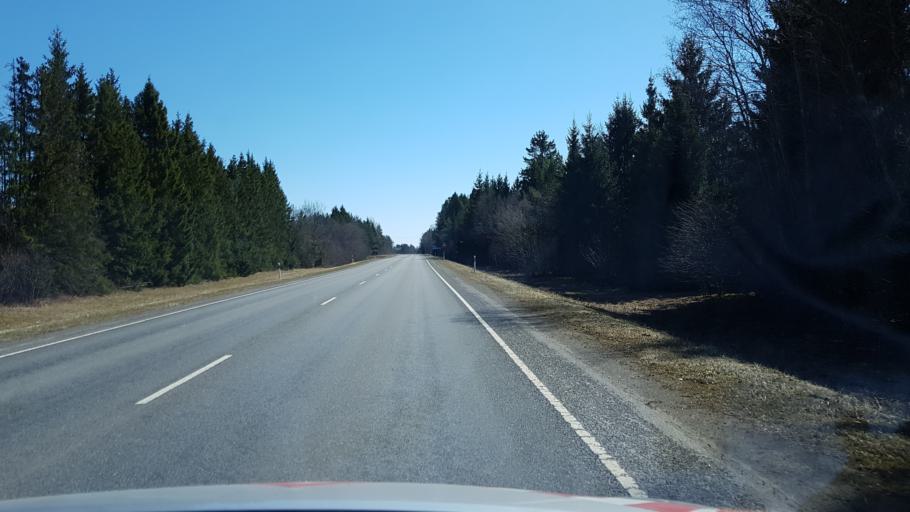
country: EE
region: Harju
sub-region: Nissi vald
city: Turba
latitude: 58.9365
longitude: 24.0937
